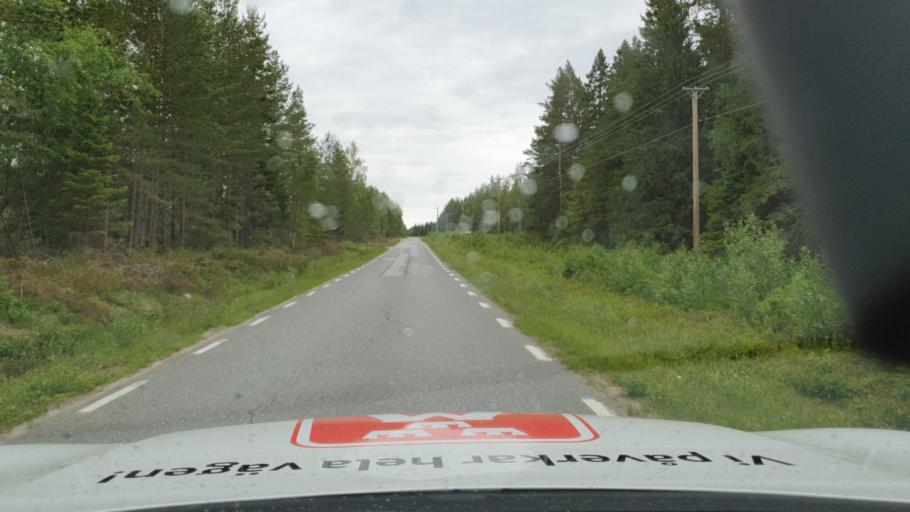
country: SE
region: Vaesterbotten
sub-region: Nordmalings Kommun
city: Nordmaling
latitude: 63.4550
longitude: 19.4673
